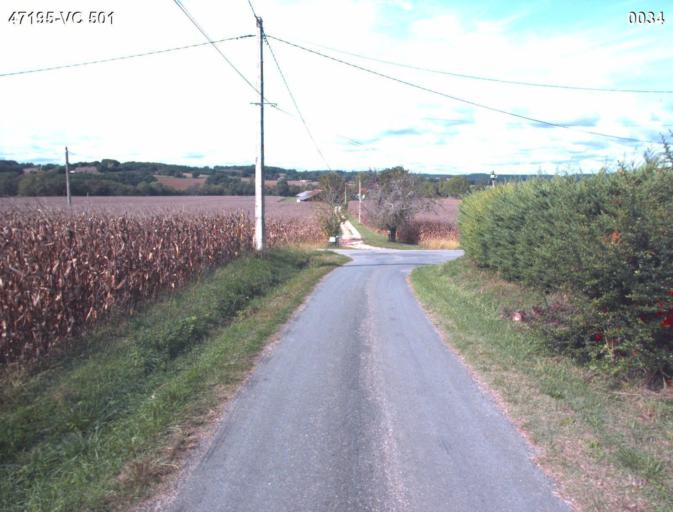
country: FR
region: Aquitaine
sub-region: Departement du Lot-et-Garonne
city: Nerac
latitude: 44.1042
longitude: 0.3103
